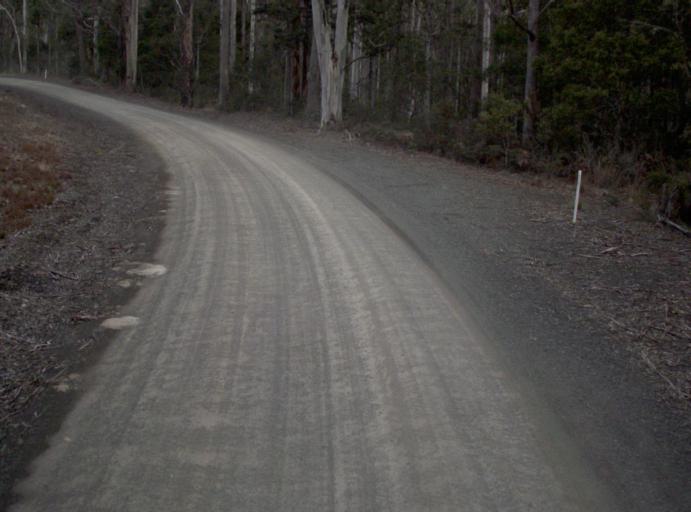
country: AU
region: Tasmania
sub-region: Launceston
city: Newstead
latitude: -41.3026
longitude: 147.3325
